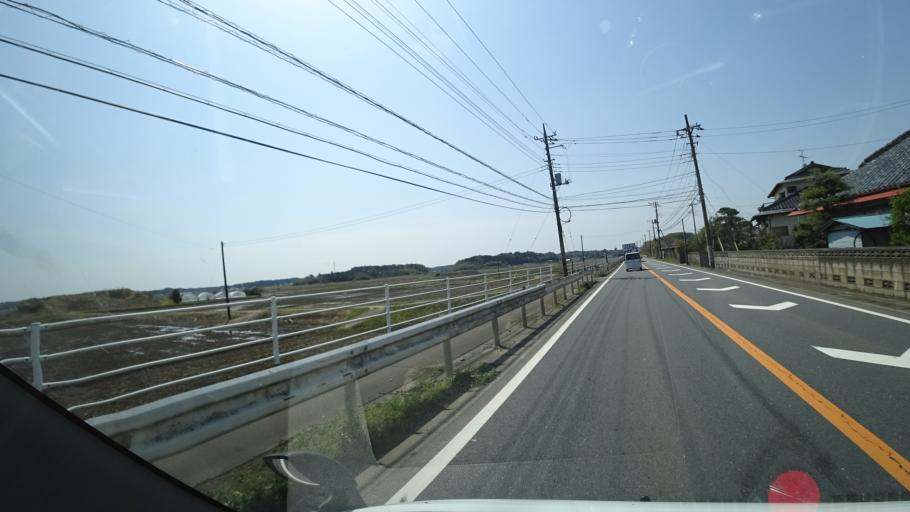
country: JP
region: Chiba
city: Narita
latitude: 35.8343
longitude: 140.3049
